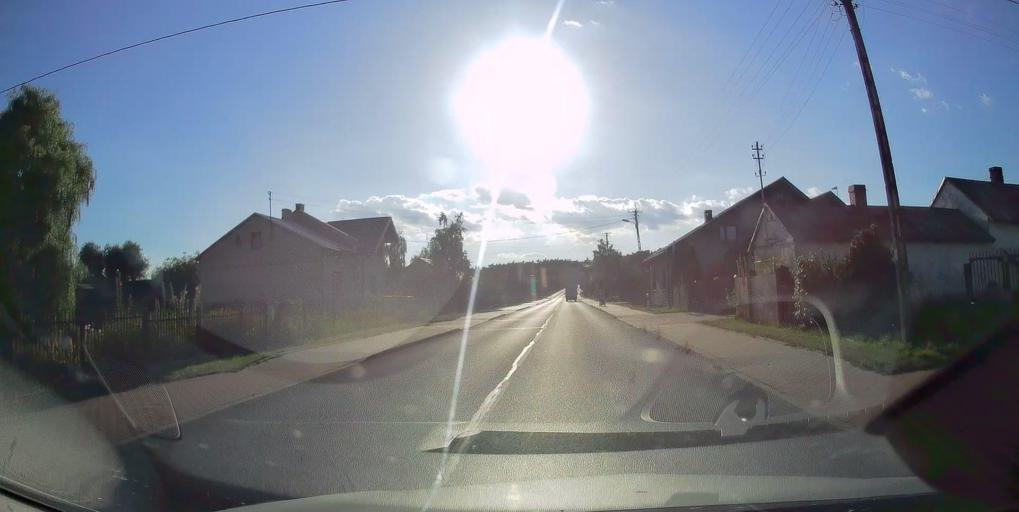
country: PL
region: Lodz Voivodeship
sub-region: Powiat rawski
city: Biala Rawska
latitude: 51.7990
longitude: 20.5243
